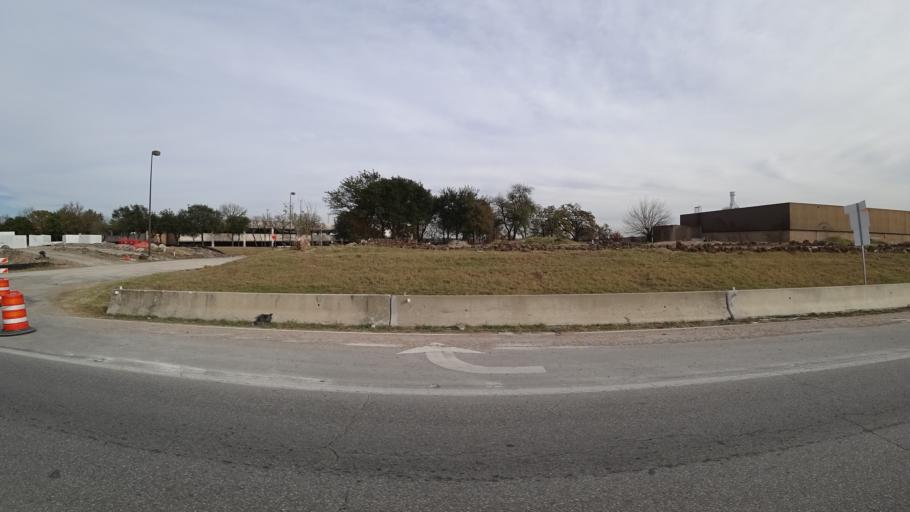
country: US
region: Texas
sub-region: Travis County
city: Austin
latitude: 30.2698
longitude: -97.6694
